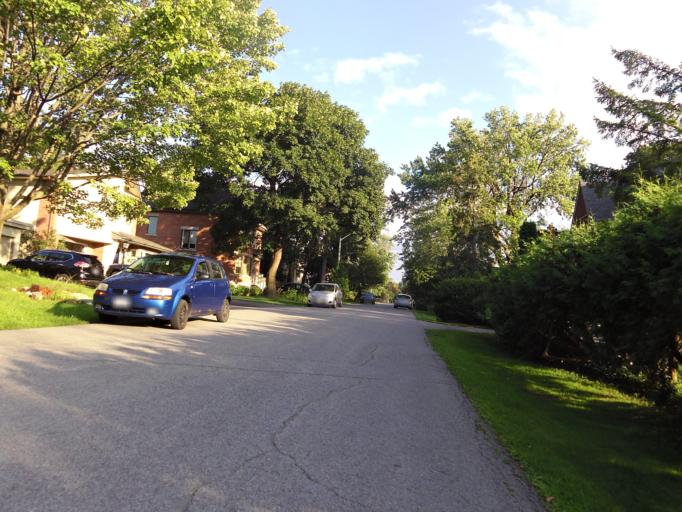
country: CA
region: Ontario
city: Ottawa
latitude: 45.3874
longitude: -75.7648
